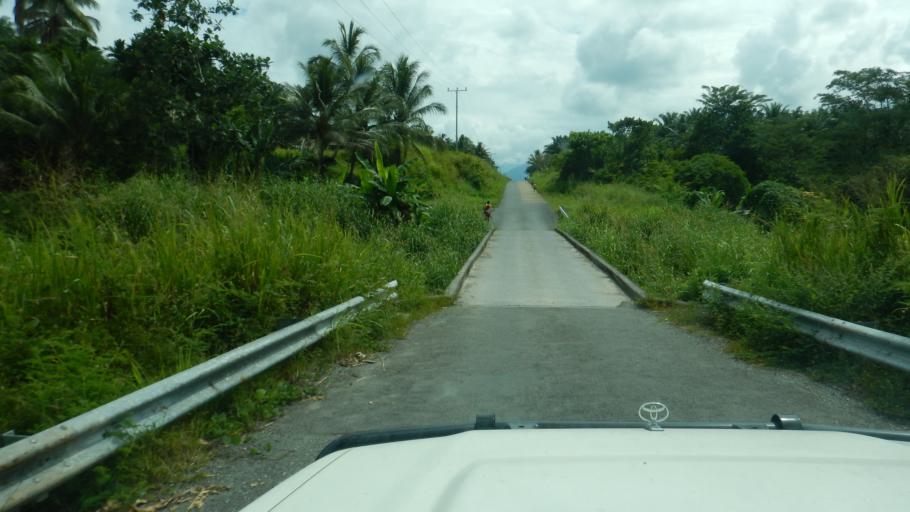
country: PG
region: Northern Province
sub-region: Sohe
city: Popondetta
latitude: -8.8300
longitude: 148.0549
